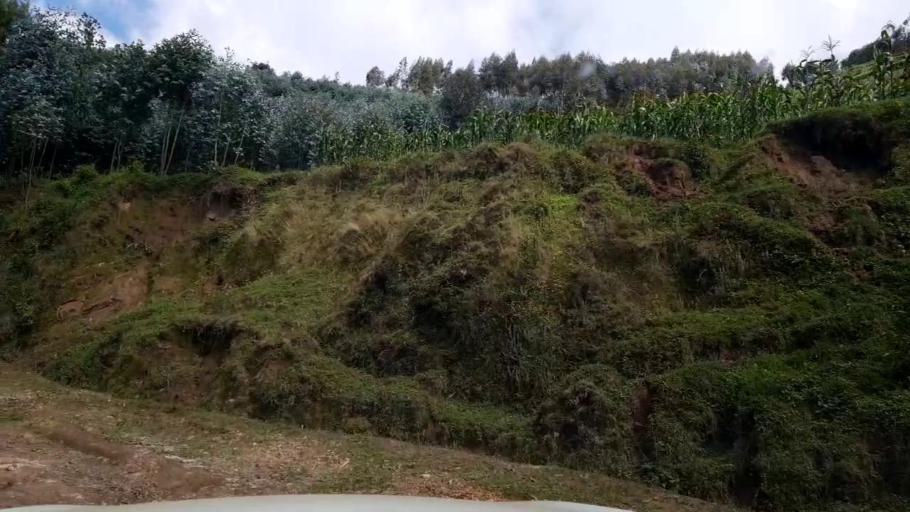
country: RW
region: Western Province
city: Kibuye
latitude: -1.8801
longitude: 29.4727
